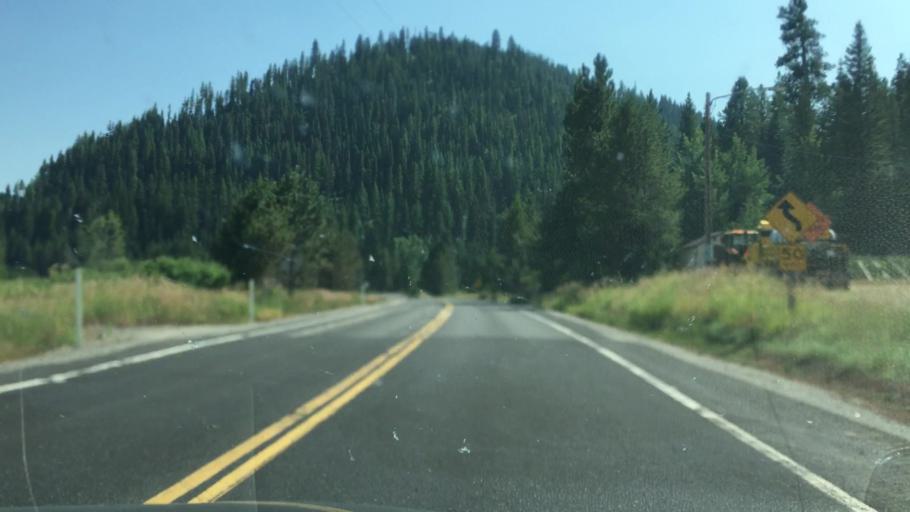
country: US
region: Idaho
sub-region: Valley County
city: Cascade
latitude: 44.3009
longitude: -116.0891
